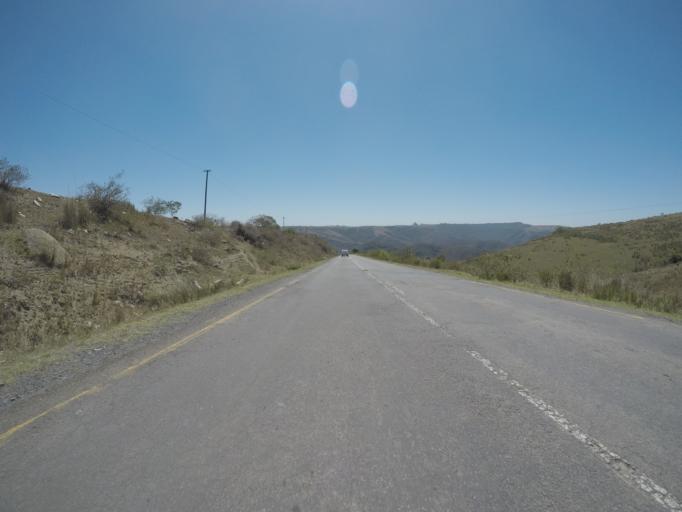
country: ZA
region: Eastern Cape
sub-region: OR Tambo District Municipality
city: Mthatha
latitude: -31.9193
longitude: 28.9672
